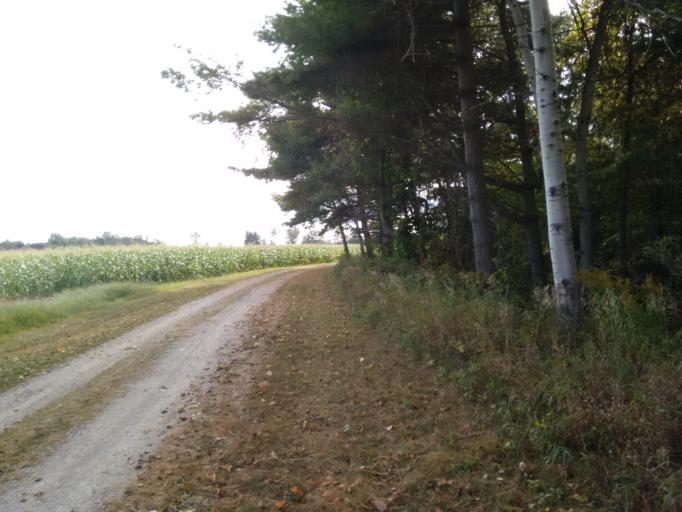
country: CA
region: Ontario
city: St. Thomas
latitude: 42.7296
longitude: -81.2115
